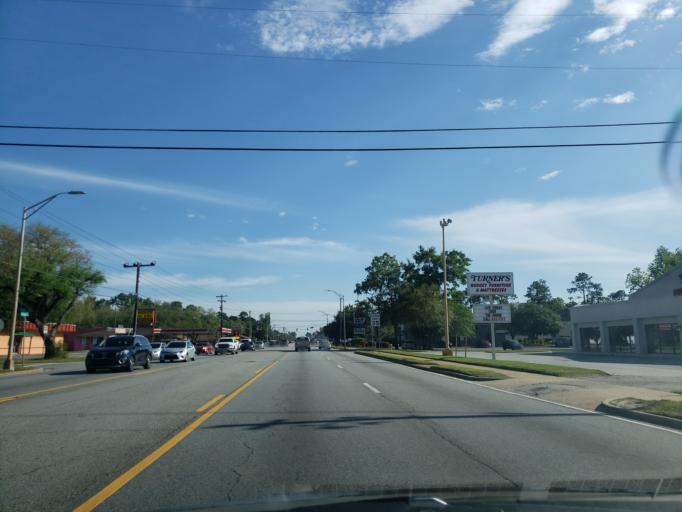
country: US
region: Georgia
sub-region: Dougherty County
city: Albany
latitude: 31.5989
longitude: -84.1760
